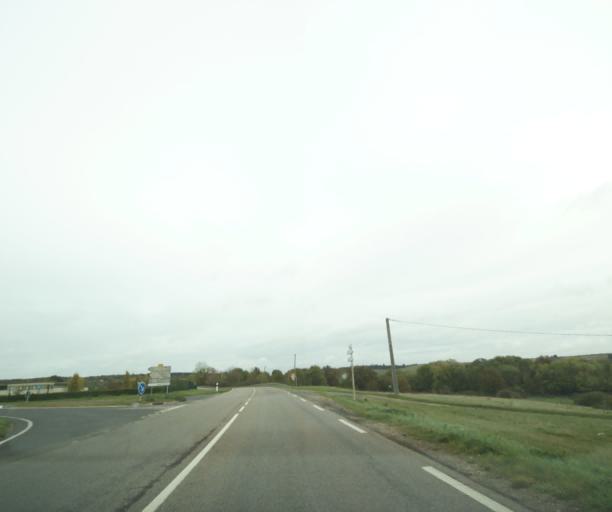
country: FR
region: Centre
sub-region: Departement d'Eure-et-Loir
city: Cherisy
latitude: 48.7587
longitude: 1.3970
